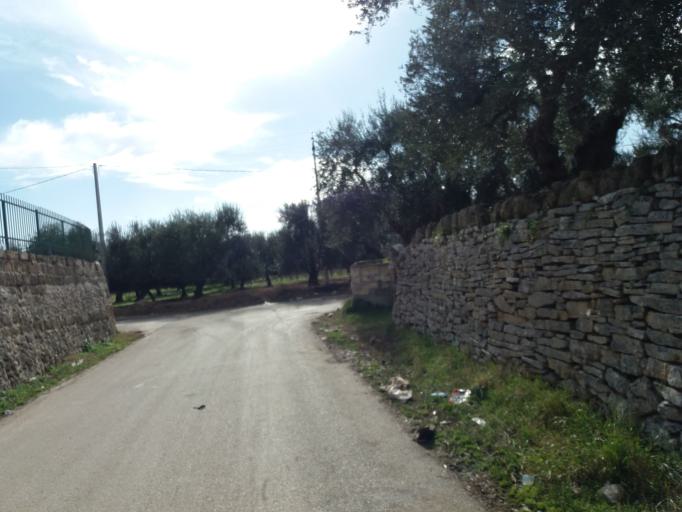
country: IT
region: Apulia
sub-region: Provincia di Barletta - Andria - Trani
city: Andria
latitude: 41.2143
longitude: 16.3085
